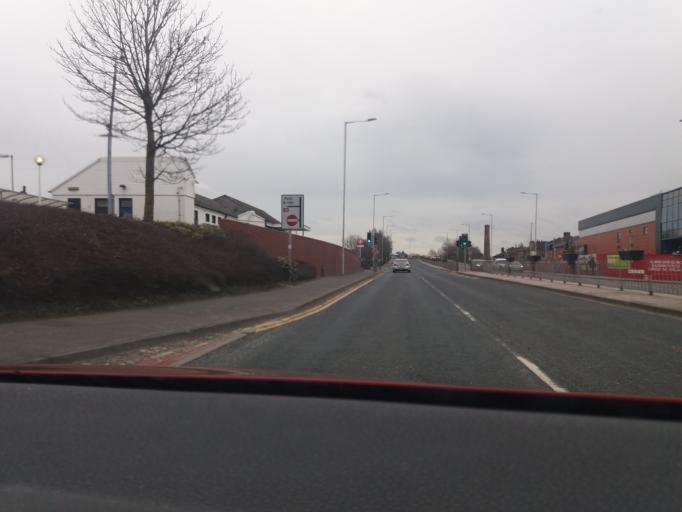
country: GB
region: England
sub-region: Lancashire
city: Chorley
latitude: 53.6529
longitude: -2.6274
